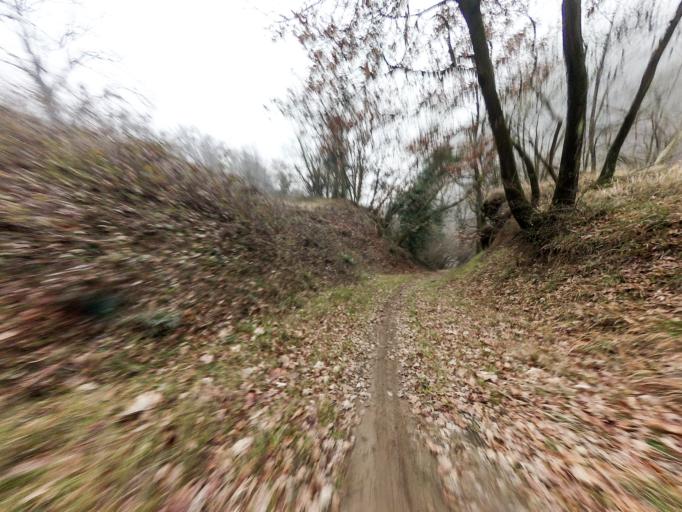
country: IT
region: Emilia-Romagna
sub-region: Provincia di Bologna
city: Pianoro
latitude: 44.3416
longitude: 11.3198
